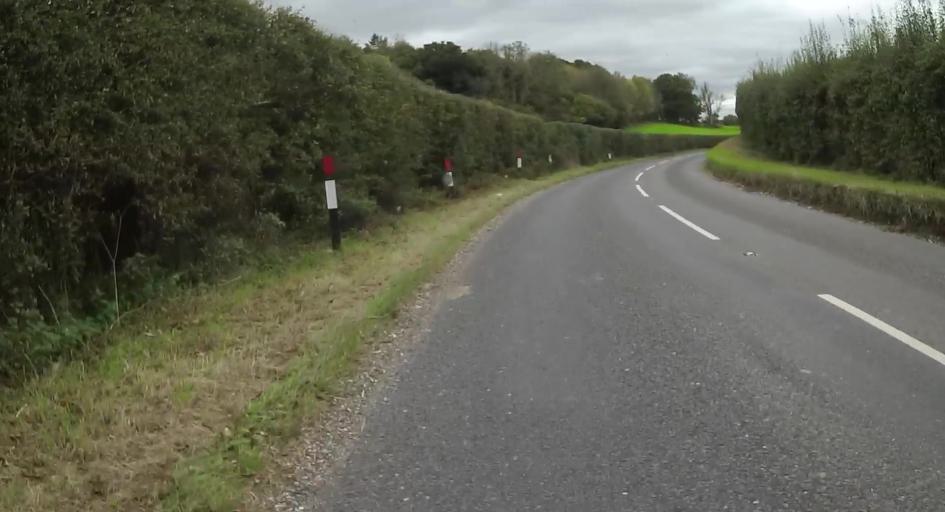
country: GB
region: England
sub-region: Hampshire
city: Basingstoke
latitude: 51.1993
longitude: -1.1228
